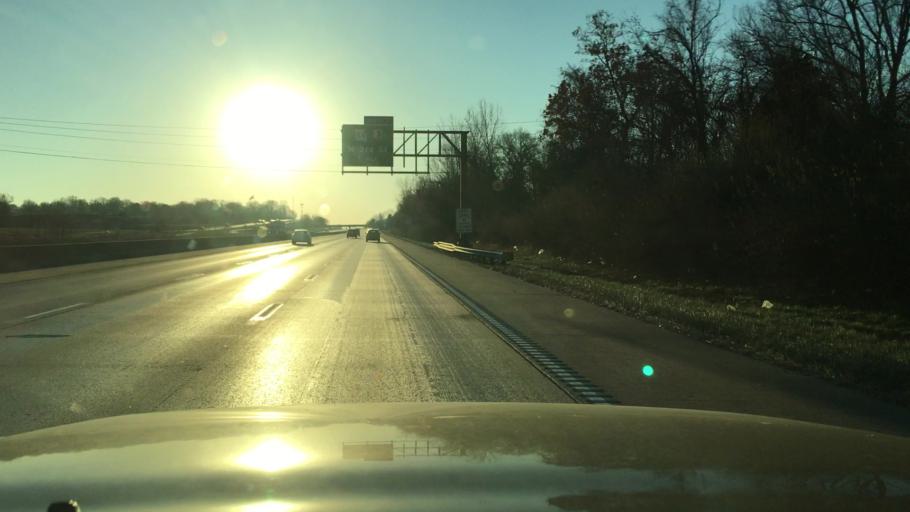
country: US
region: Missouri
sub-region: Saint Charles County
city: Saint Charles
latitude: 38.8141
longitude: -90.4920
